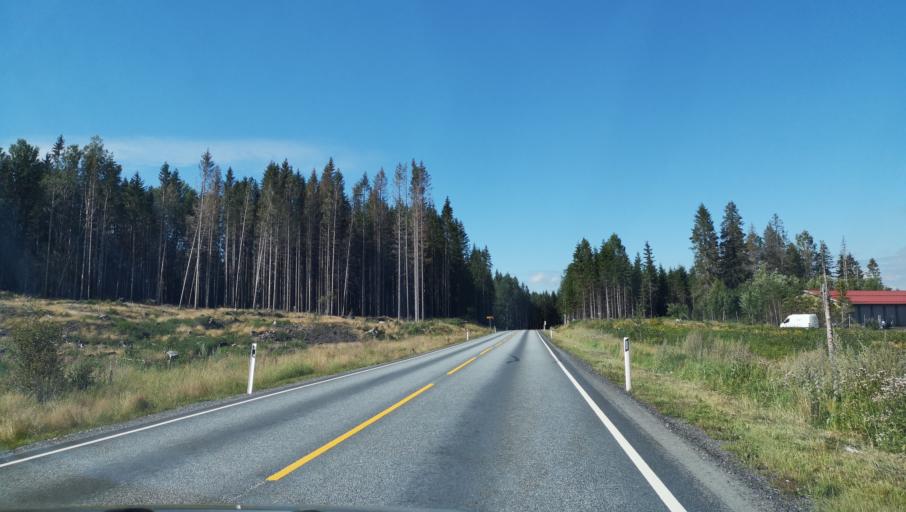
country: NO
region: Ostfold
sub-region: Valer
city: Kirkebygda
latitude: 59.5787
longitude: 10.8750
